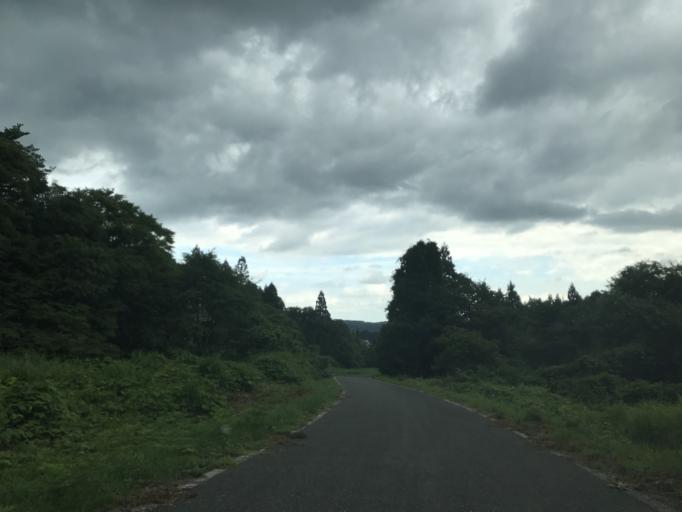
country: JP
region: Iwate
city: Ichinoseki
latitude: 38.9557
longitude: 141.0452
